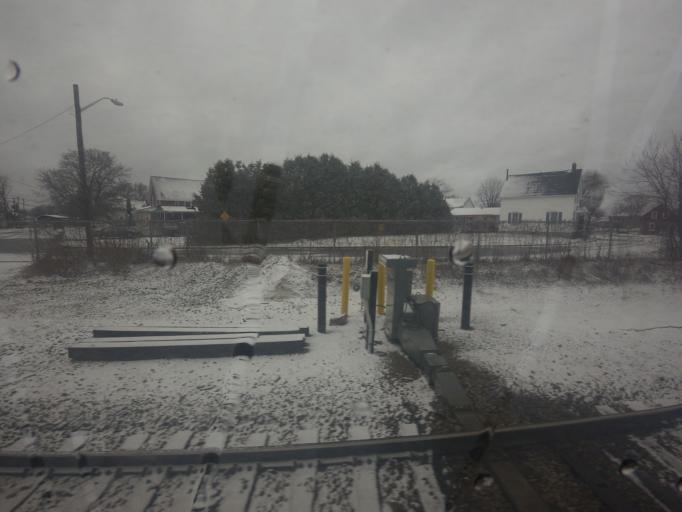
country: CA
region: Ontario
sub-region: Lanark County
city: Smiths Falls
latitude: 44.9082
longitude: -76.0205
